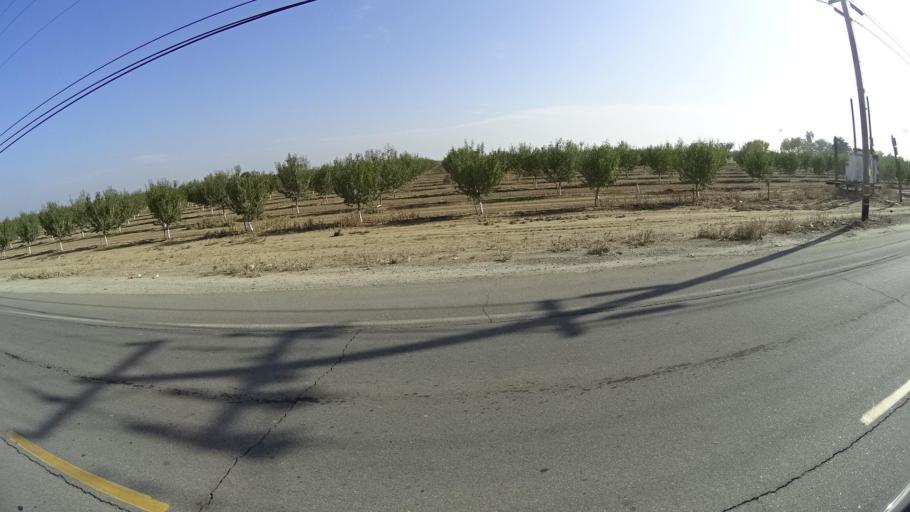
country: US
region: California
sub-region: Kern County
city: McFarland
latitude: 35.6868
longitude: -119.2231
